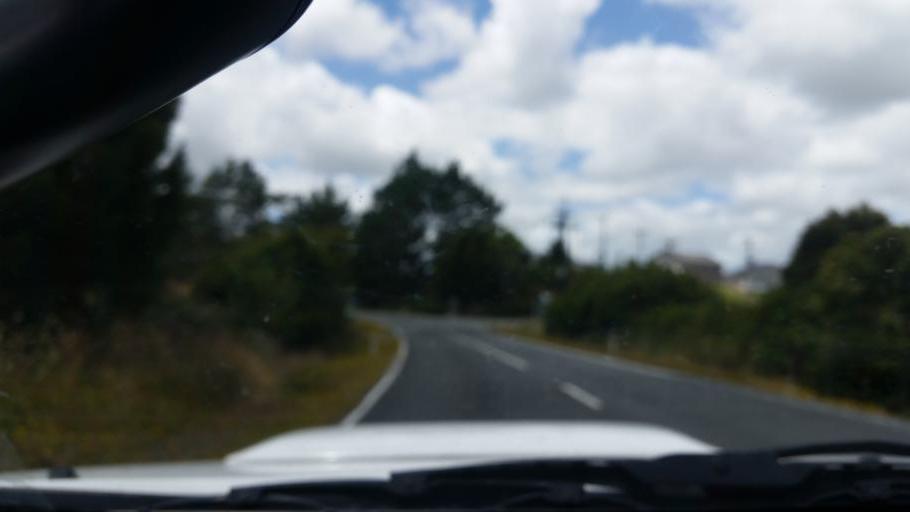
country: NZ
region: Northland
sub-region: Whangarei
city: Ruakaka
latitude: -36.0715
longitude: 174.2649
